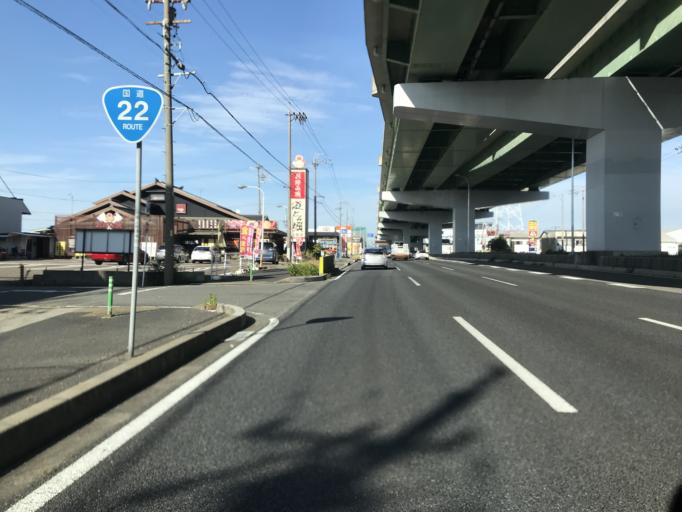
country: JP
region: Aichi
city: Iwakura
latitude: 35.2504
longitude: 136.8441
